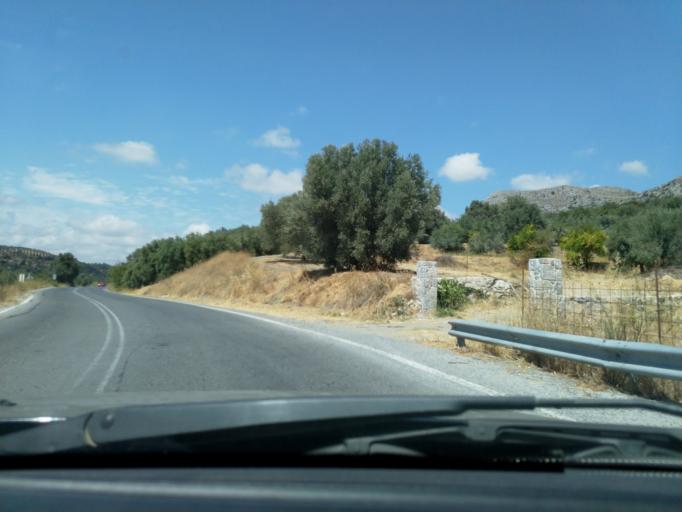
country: GR
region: Crete
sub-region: Nomos Rethymnis
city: Agia Foteini
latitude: 35.1940
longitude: 24.5510
